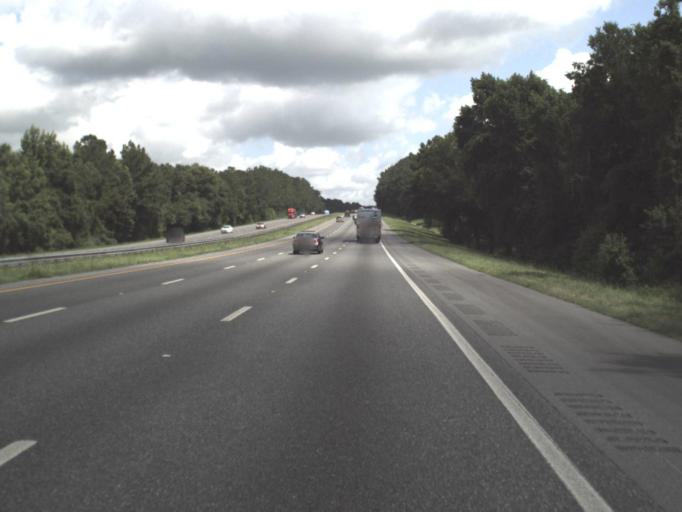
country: US
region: Florida
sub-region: Alachua County
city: High Springs
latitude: 29.9324
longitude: -82.5611
